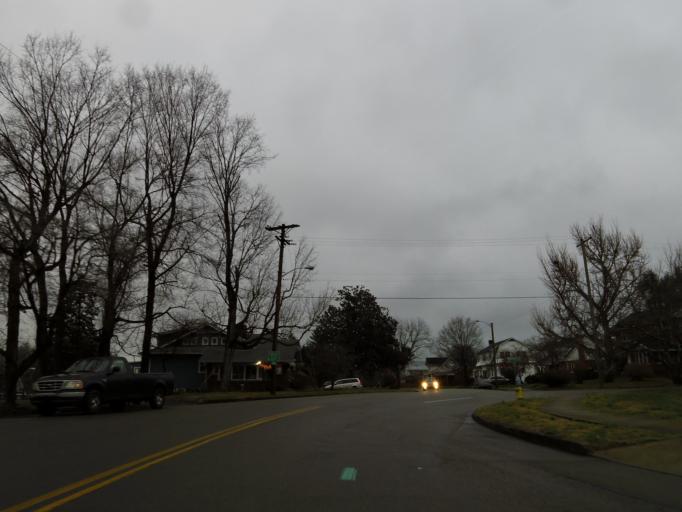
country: US
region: Tennessee
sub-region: Knox County
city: Knoxville
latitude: 35.9599
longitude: -83.8879
